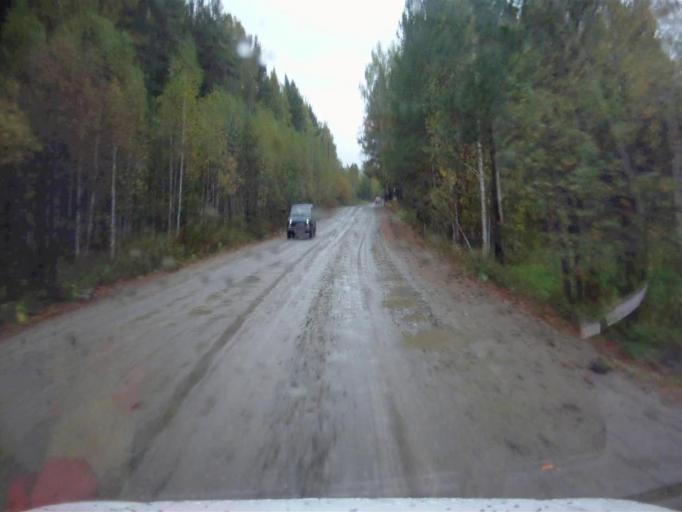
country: RU
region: Chelyabinsk
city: Kyshtym
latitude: 55.7516
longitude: 60.4868
